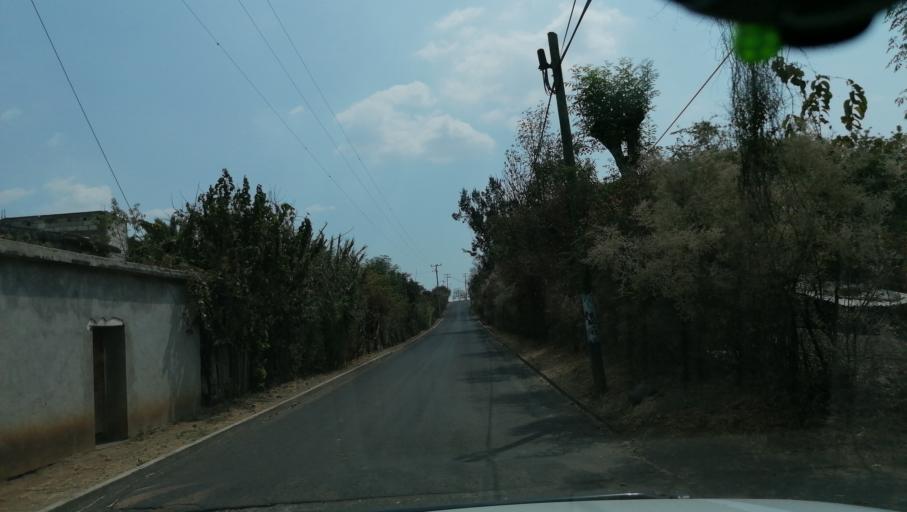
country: MX
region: Morelos
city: Tlacotepec
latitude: 18.8185
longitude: -98.7056
